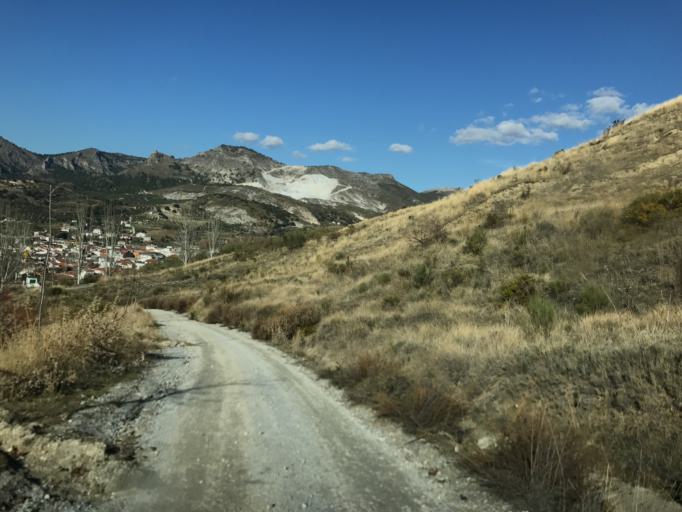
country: ES
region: Andalusia
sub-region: Provincia de Granada
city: Beas de Granada
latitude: 37.2132
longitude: -3.4786
